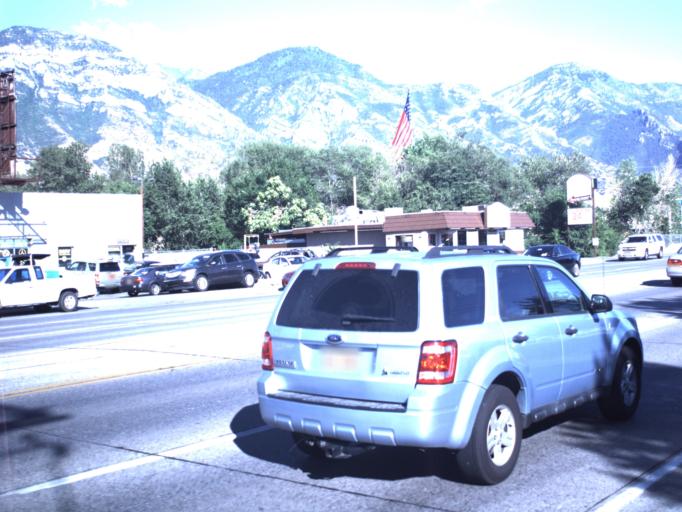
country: US
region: Utah
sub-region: Utah County
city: Provo
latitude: 40.2534
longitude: -111.6698
